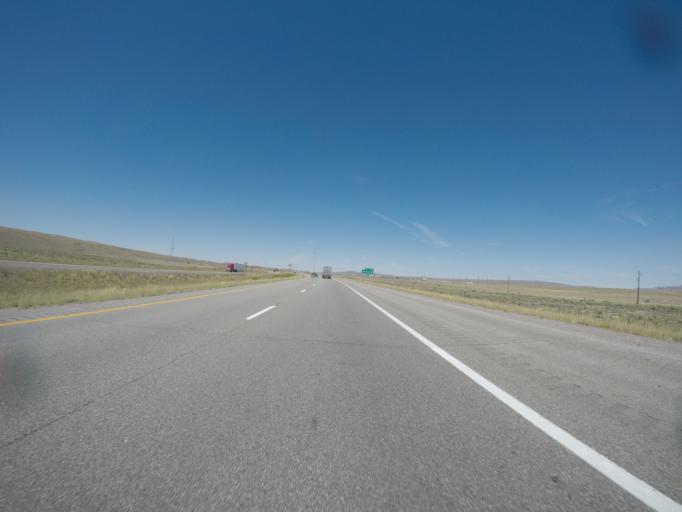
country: US
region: Wyoming
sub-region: Carbon County
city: Rawlins
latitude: 41.7735
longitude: -107.0706
